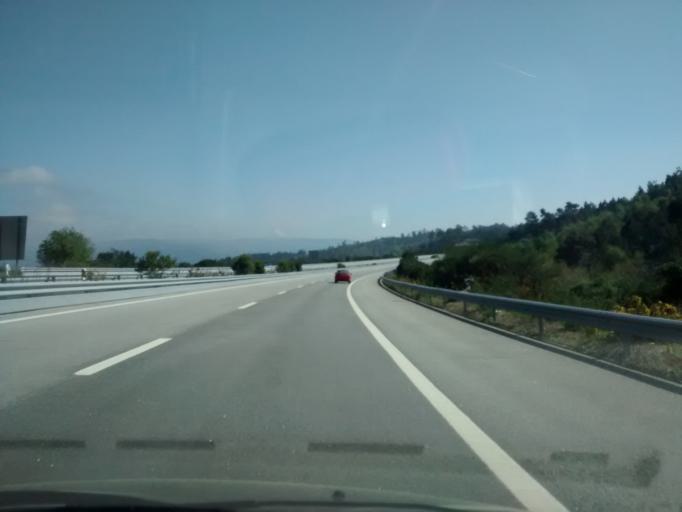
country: PT
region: Braga
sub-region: Cabeceiras de Basto
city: Refojos de Basto
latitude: 41.4606
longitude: -8.0300
